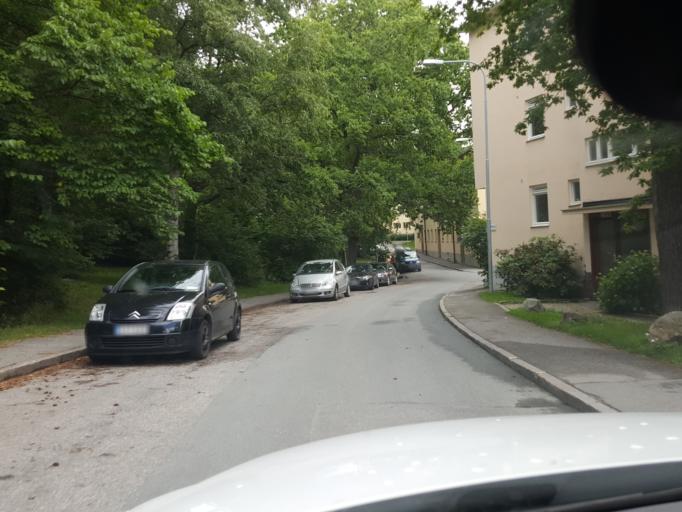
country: SE
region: Stockholm
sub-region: Stockholms Kommun
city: Bromma
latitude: 59.3210
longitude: 17.9735
